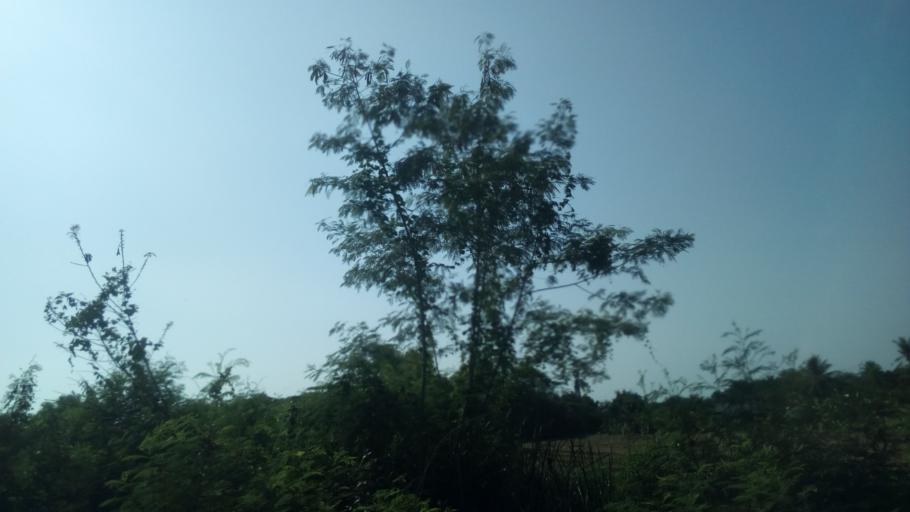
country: TH
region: Nonthaburi
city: Sai Noi
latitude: 13.9391
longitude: 100.3251
